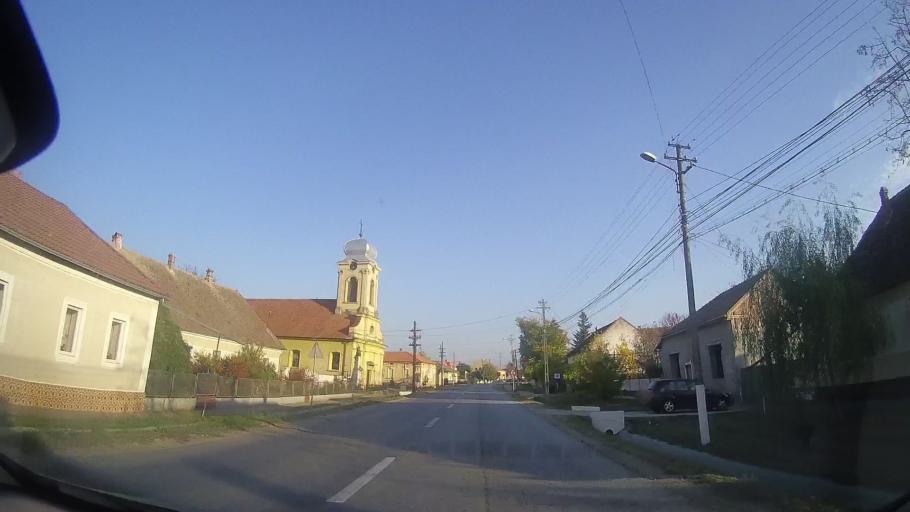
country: RO
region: Timis
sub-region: Comuna Pischia
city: Pischia
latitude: 45.9016
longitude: 21.3401
